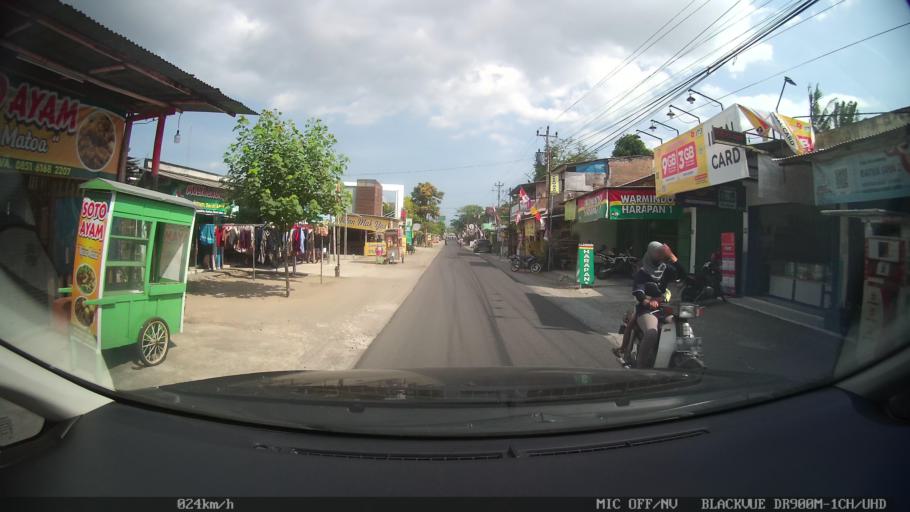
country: ID
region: Daerah Istimewa Yogyakarta
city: Kasihan
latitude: -7.8203
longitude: 110.3282
